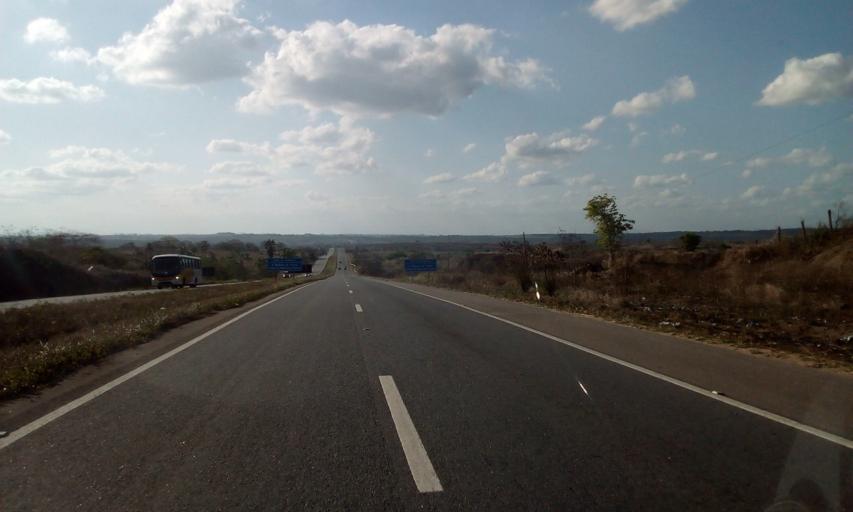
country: BR
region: Paraiba
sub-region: Cruz Do Espirito Santo
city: Cruz do Espirito Santo
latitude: -7.1984
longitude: -35.1658
